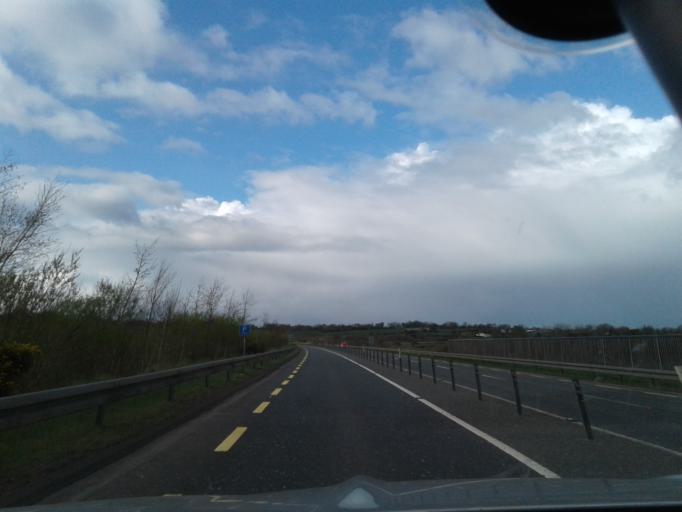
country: IE
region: Ulster
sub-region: County Monaghan
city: Castleblayney
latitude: 54.1711
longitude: -6.8109
